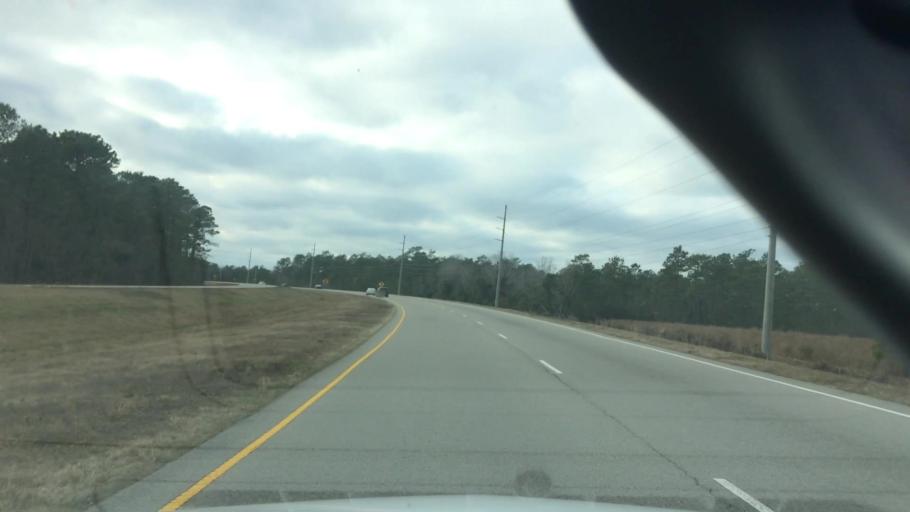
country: US
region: North Carolina
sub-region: Brunswick County
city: Shallotte
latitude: 33.9895
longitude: -78.3839
